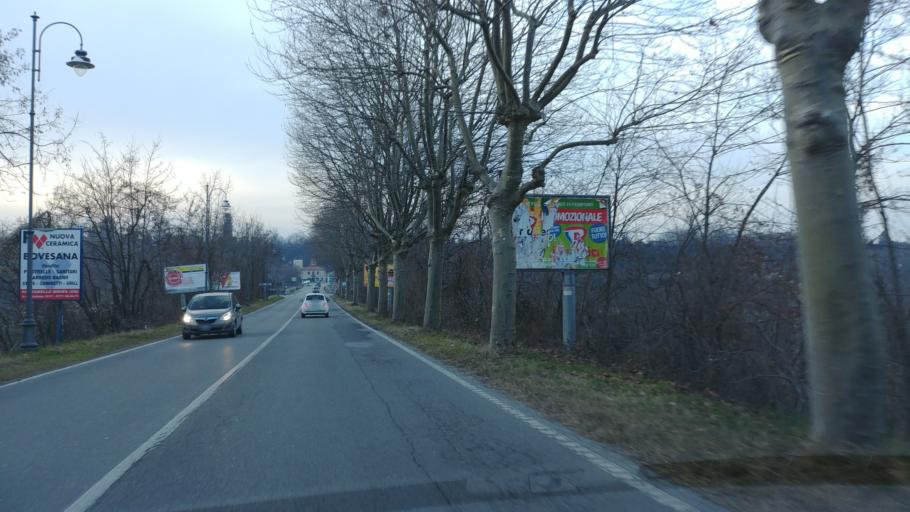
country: IT
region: Piedmont
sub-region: Provincia di Cuneo
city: Cuneo
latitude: 44.3973
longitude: 7.5473
